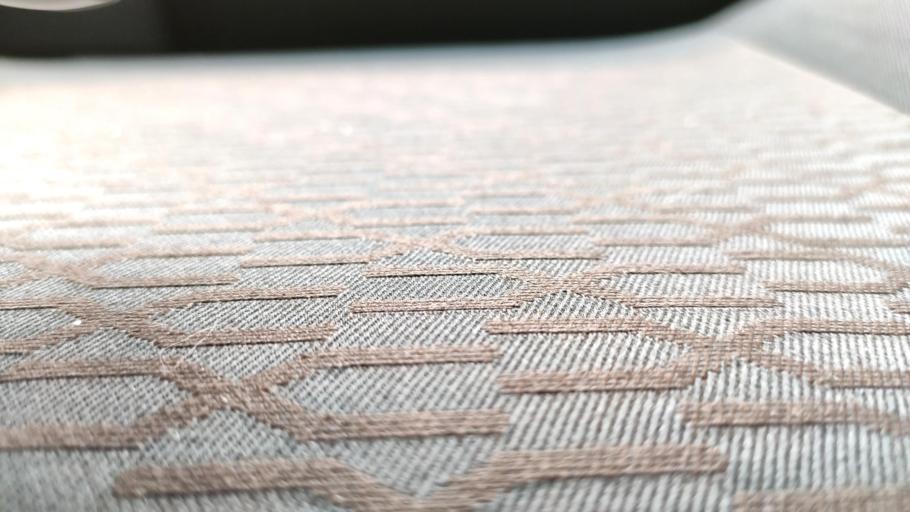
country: RU
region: Perm
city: Perm
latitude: 58.0044
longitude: 56.1883
